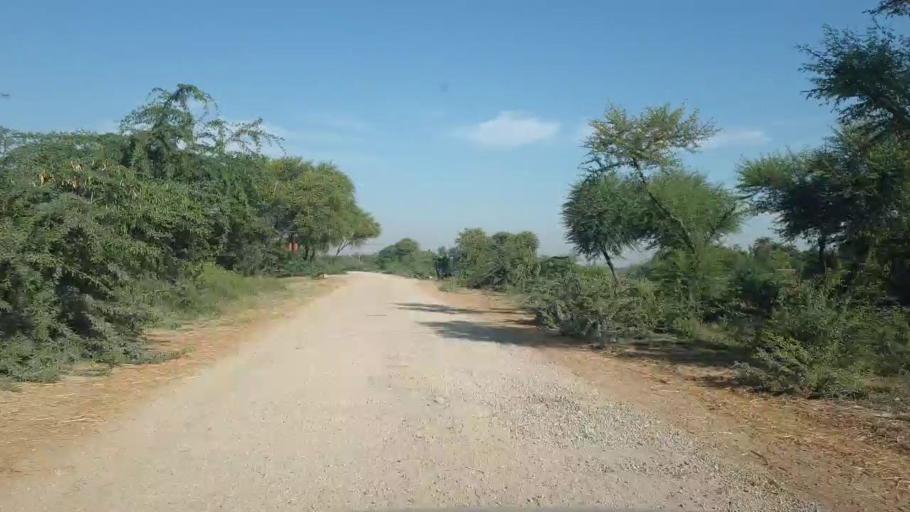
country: PK
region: Sindh
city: Talhar
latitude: 24.9400
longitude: 68.7892
